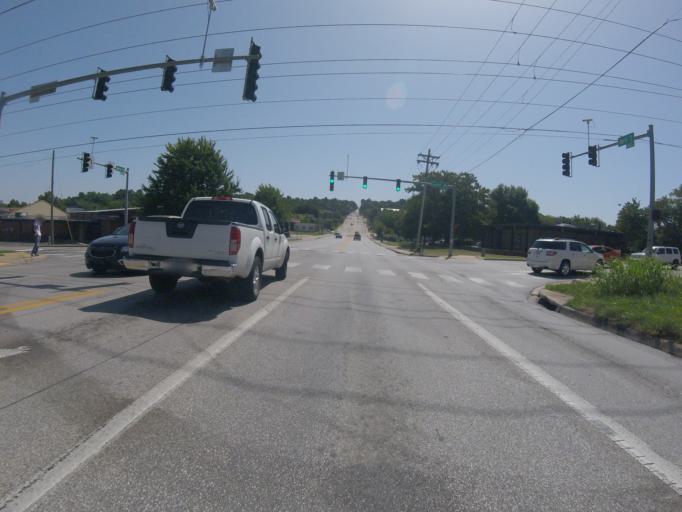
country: US
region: Arkansas
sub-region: Washington County
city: Fayetteville
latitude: 36.0775
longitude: -94.1712
